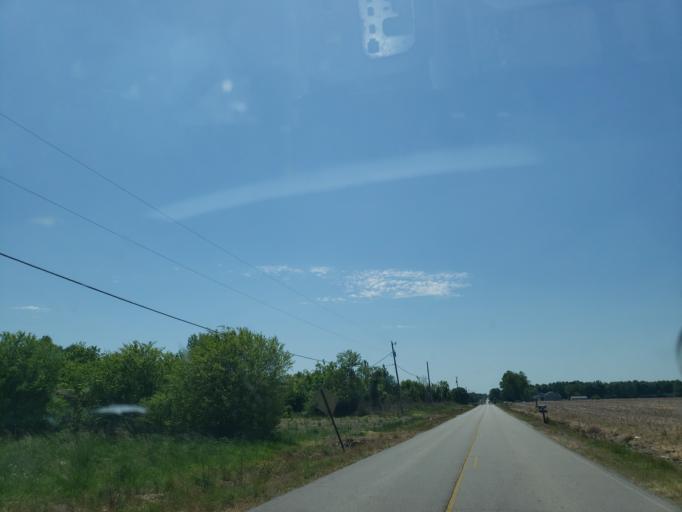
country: US
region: Alabama
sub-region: Madison County
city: Harvest
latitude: 34.9616
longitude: -86.7255
